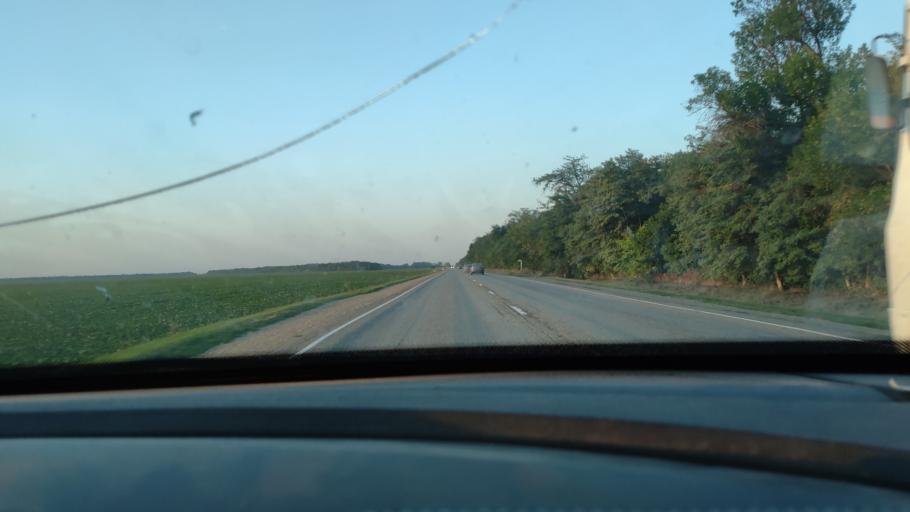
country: RU
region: Krasnodarskiy
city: Starominskaya
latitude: 46.4542
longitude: 39.0324
